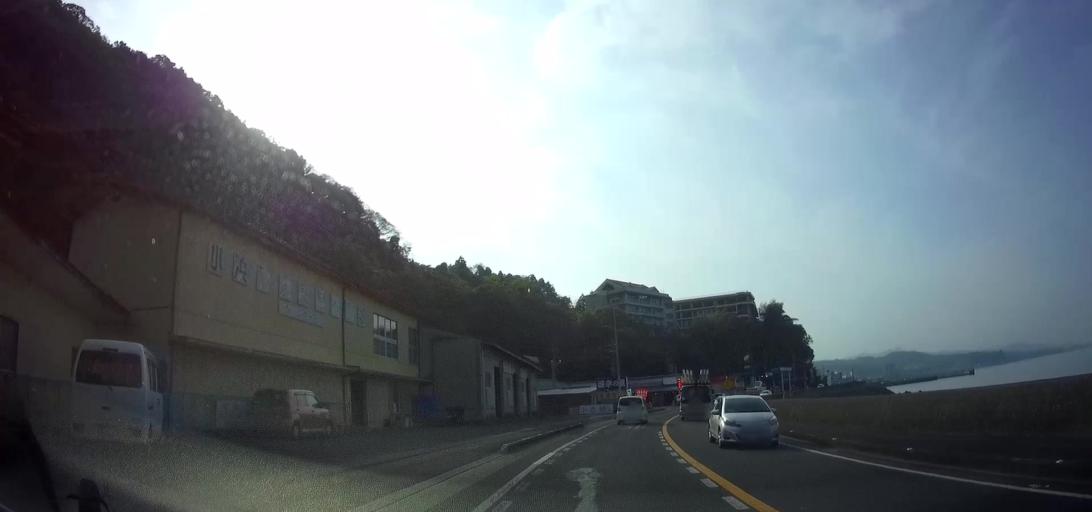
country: JP
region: Nagasaki
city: Shimabara
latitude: 32.7384
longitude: 130.2100
